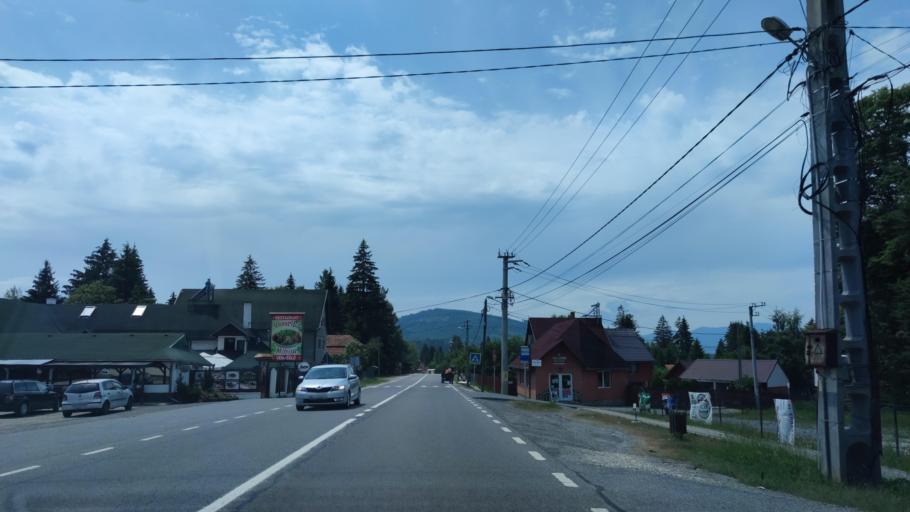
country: RO
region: Harghita
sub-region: Comuna Sandominic
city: Sandominic
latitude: 46.6233
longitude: 25.7144
